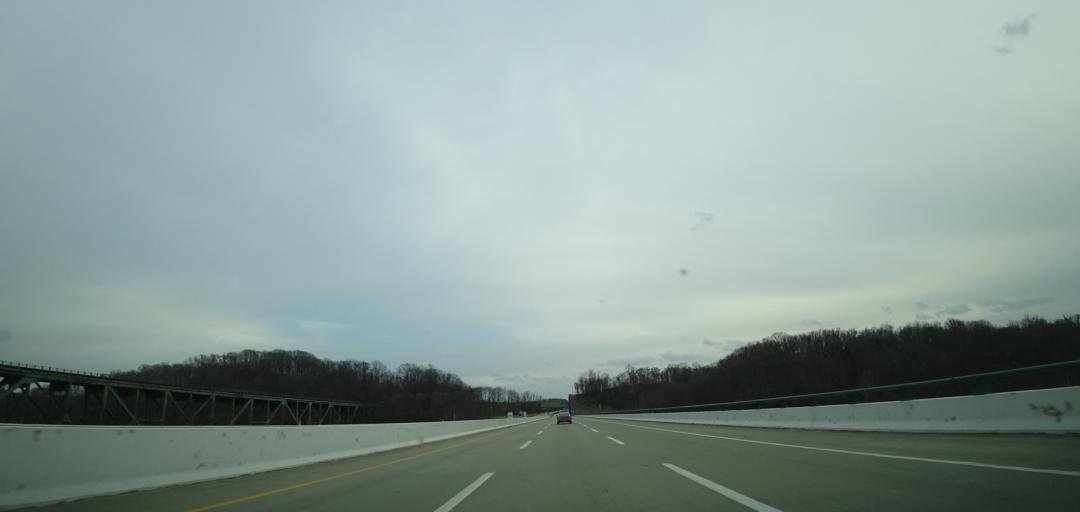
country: US
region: Pennsylvania
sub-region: Allegheny County
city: Cheswick
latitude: 40.5376
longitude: -79.8226
